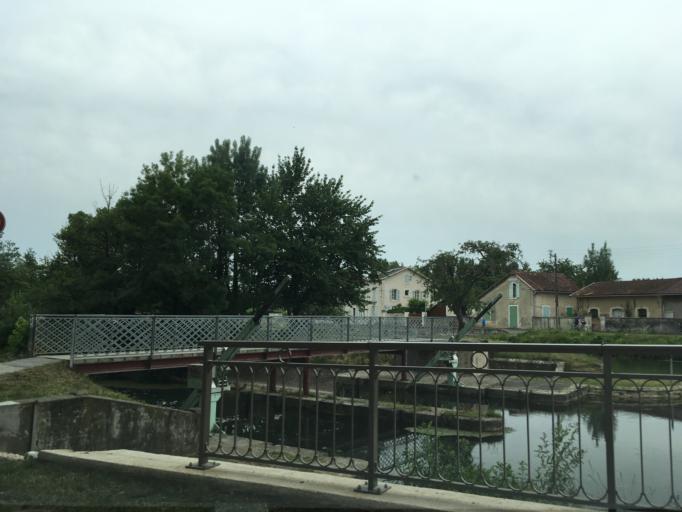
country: FR
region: Poitou-Charentes
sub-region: Departement des Deux-Sevres
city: Niort
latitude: 46.3290
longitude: -0.4775
